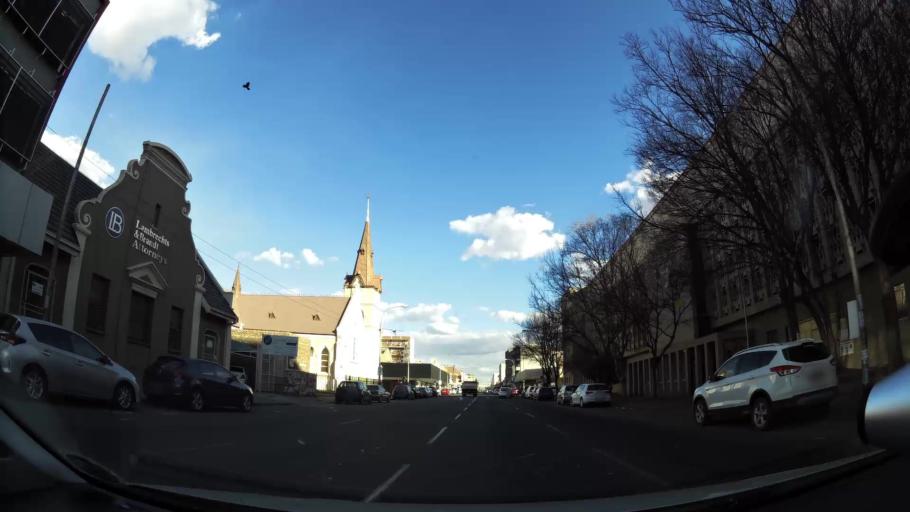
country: ZA
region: North-West
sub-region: Dr Kenneth Kaunda District Municipality
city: Klerksdorp
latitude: -26.8659
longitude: 26.6661
